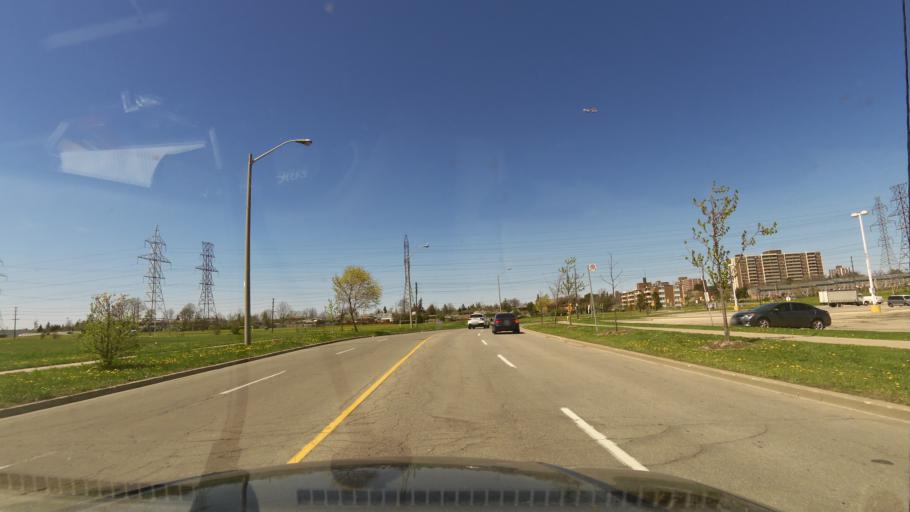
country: CA
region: Ontario
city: Concord
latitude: 43.7581
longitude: -79.5214
